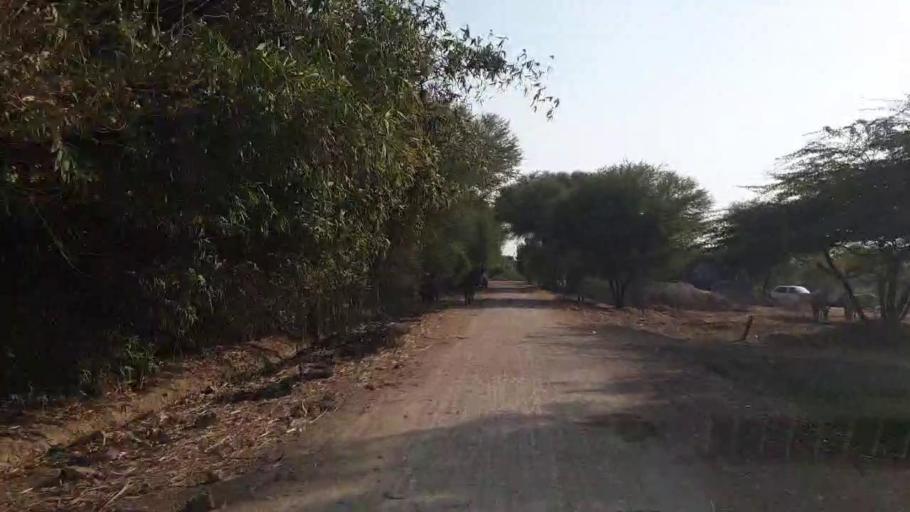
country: PK
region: Sindh
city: Mirpur Khas
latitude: 25.4098
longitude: 68.9438
